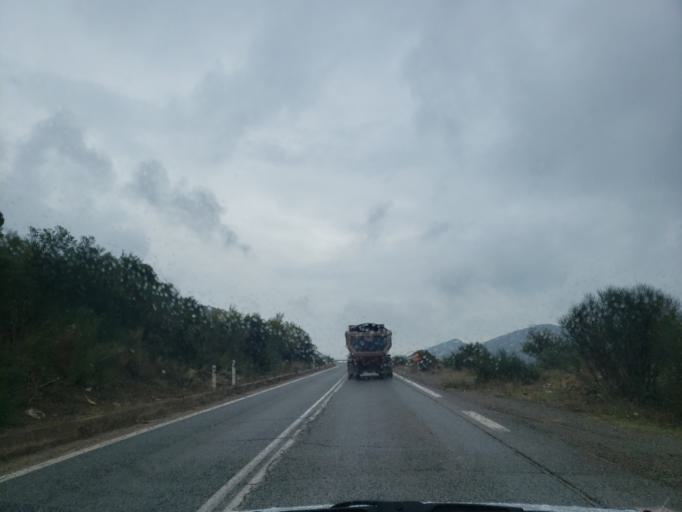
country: GR
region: Central Greece
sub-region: Nomos Fokidos
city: Amfissa
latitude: 38.5849
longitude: 22.3908
